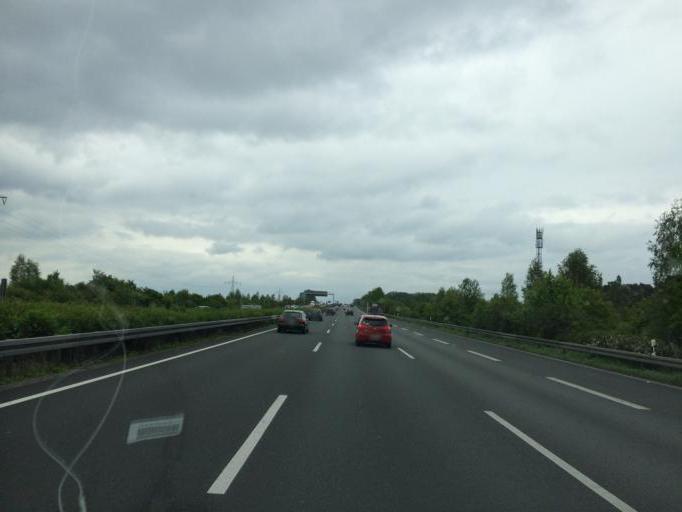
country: DE
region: Lower Saxony
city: Lehrte
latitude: 52.3810
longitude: 10.0254
